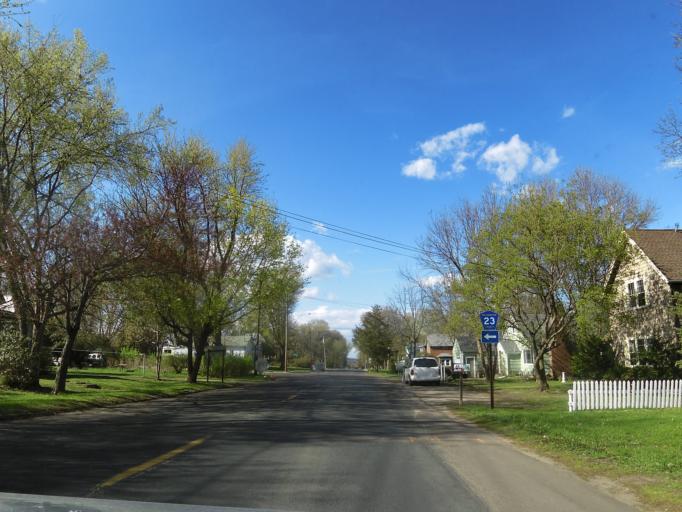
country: US
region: Minnesota
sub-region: Washington County
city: Oak Park Heights
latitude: 45.0421
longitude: -92.7999
